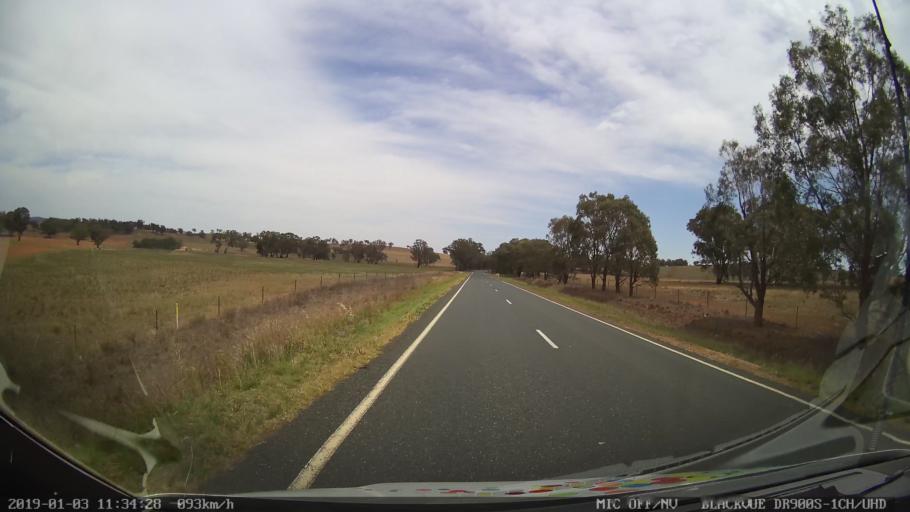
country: AU
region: New South Wales
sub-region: Weddin
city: Grenfell
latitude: -33.9346
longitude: 148.1633
